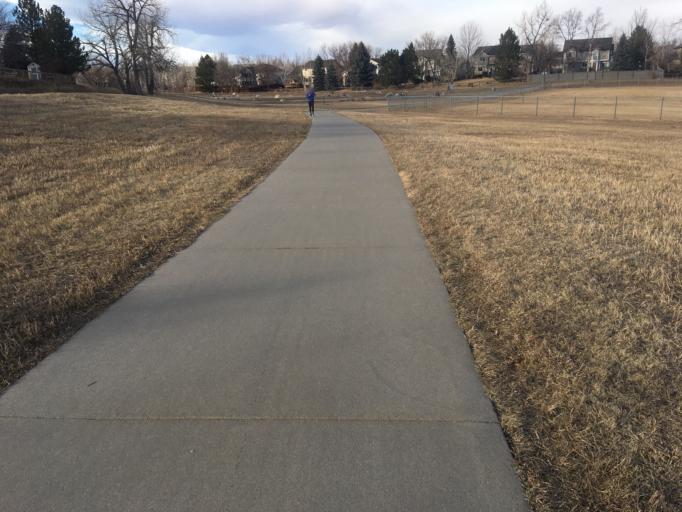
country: US
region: Colorado
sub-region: Broomfield County
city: Broomfield
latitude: 39.9362
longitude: -105.0816
